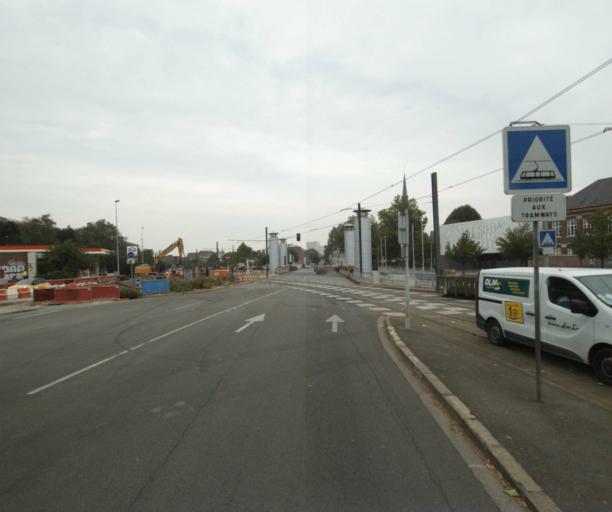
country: FR
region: Nord-Pas-de-Calais
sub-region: Departement du Nord
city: Tourcoing
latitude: 50.7128
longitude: 3.1562
